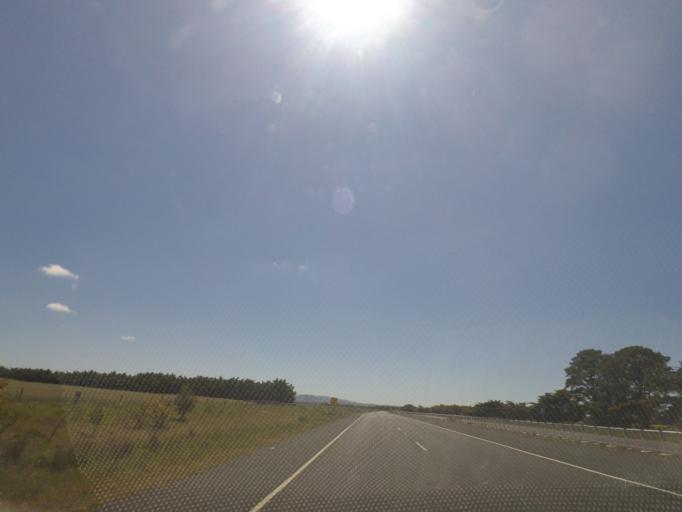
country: AU
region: Victoria
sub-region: Hume
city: Sunbury
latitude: -37.4725
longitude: 144.7480
